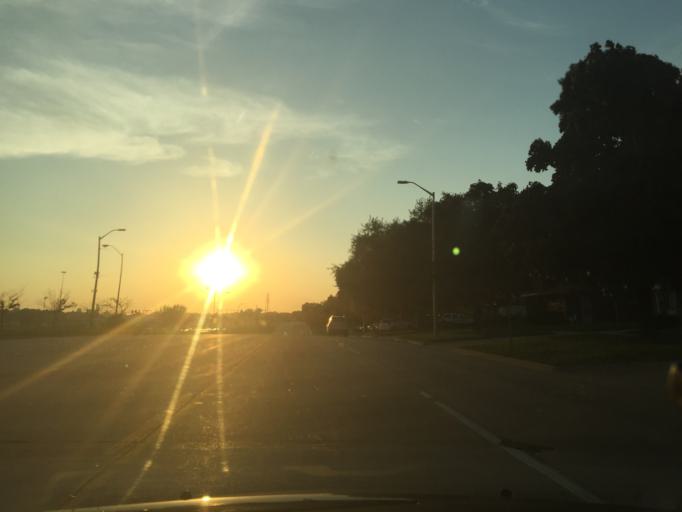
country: US
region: Michigan
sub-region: Oakland County
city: Pontiac
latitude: 42.6491
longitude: -83.2525
